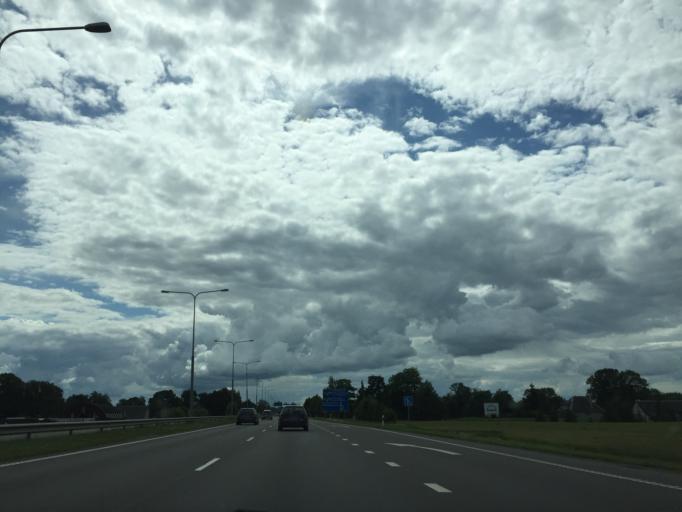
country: LT
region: Marijampoles apskritis
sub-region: Marijampole Municipality
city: Marijampole
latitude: 54.5922
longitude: 23.3899
